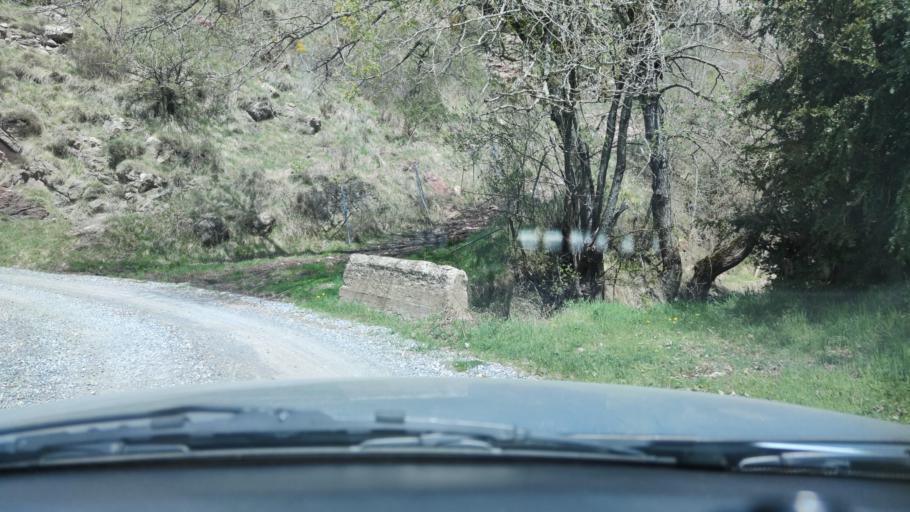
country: ES
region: Catalonia
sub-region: Provincia de Lleida
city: Sort
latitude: 42.2999
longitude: 1.1795
